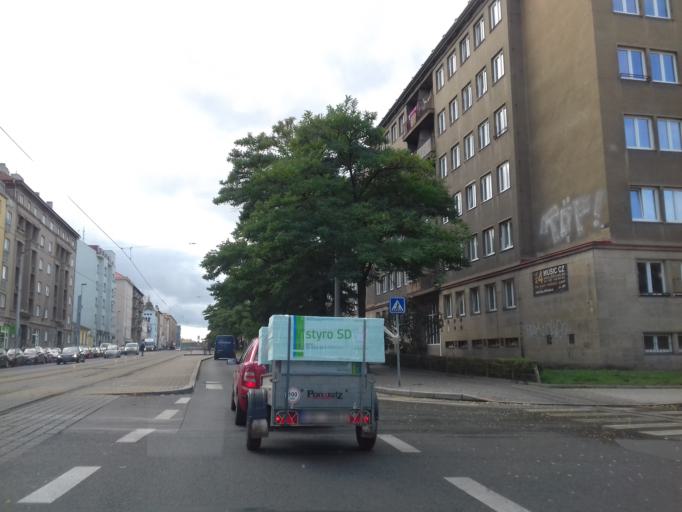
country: CZ
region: Praha
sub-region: Praha 8
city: Liben
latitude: 50.1075
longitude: 14.4904
